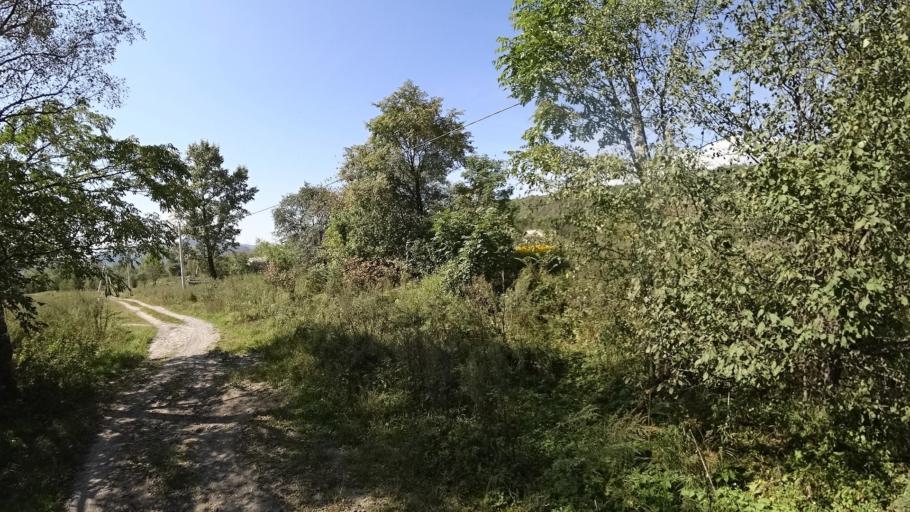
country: RU
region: Jewish Autonomous Oblast
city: Londoko
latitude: 49.0049
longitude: 131.9400
